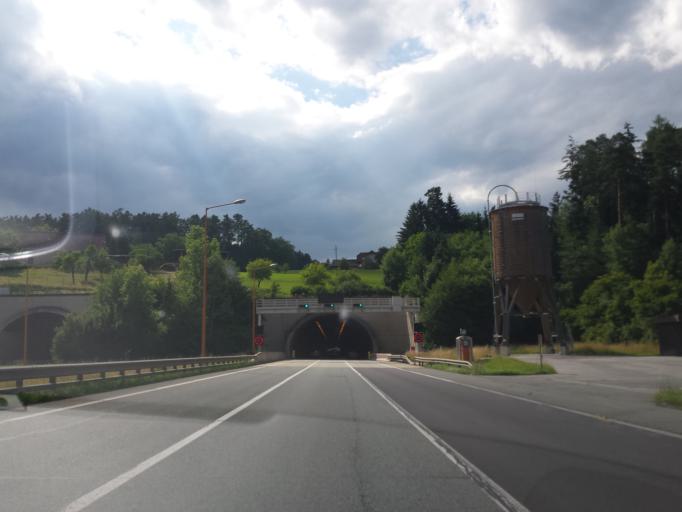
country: AT
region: Styria
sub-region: Politischer Bezirk Graz-Umgebung
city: Gratkorn
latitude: 47.1410
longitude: 15.3455
